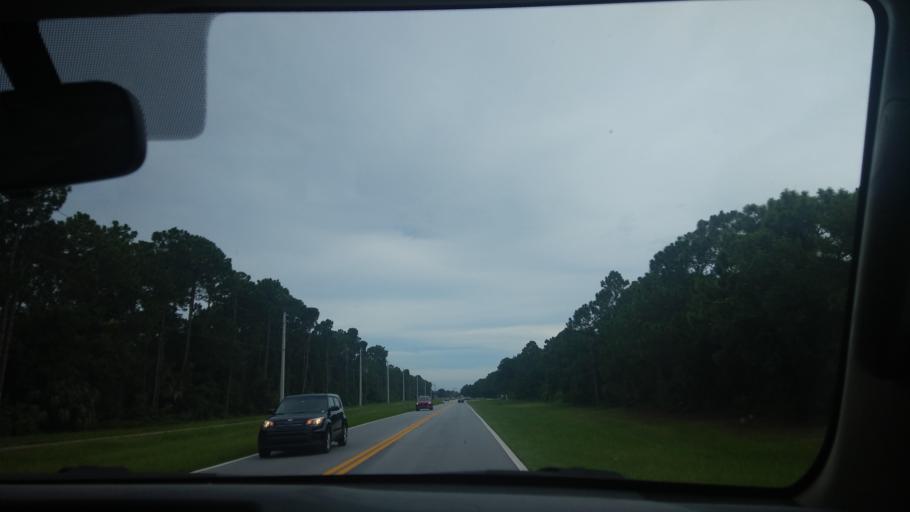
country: US
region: Florida
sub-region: Brevard County
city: Palm Bay
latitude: 27.9890
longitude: -80.6349
